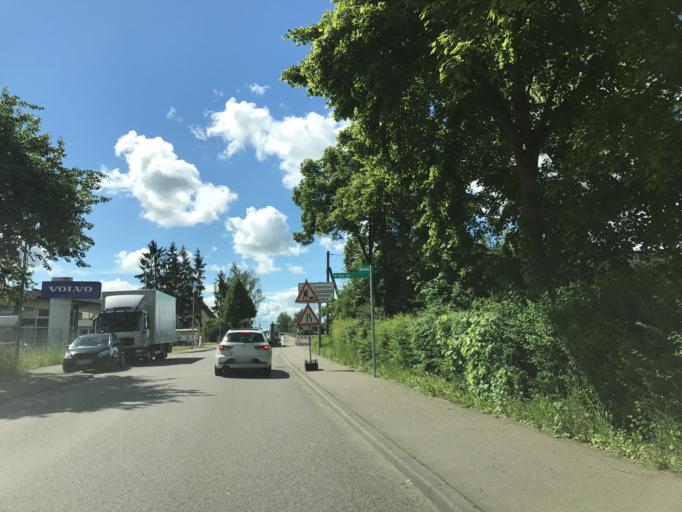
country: DE
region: Baden-Wuerttemberg
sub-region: Regierungsbezirk Stuttgart
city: Filderstadt
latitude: 48.6975
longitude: 9.2162
